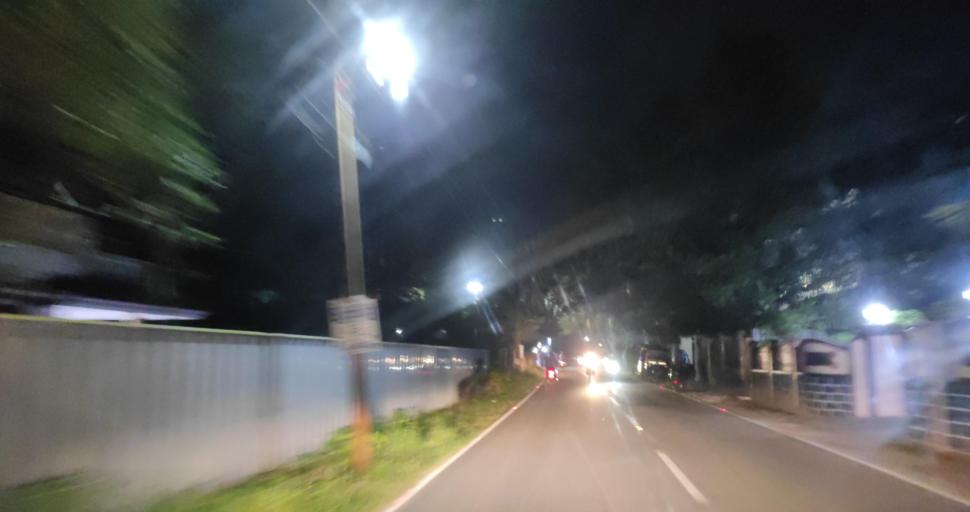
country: IN
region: Kerala
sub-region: Alappuzha
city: Vayalar
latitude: 9.6808
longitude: 76.3199
